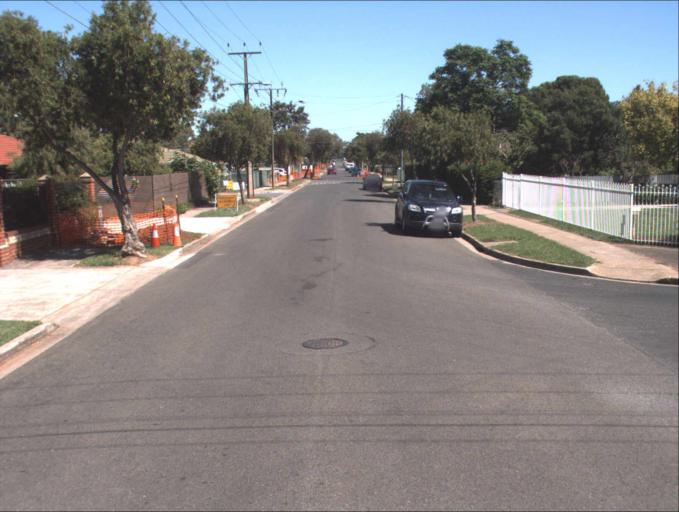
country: AU
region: South Australia
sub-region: Port Adelaide Enfield
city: Klemzig
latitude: -34.8822
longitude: 138.6441
